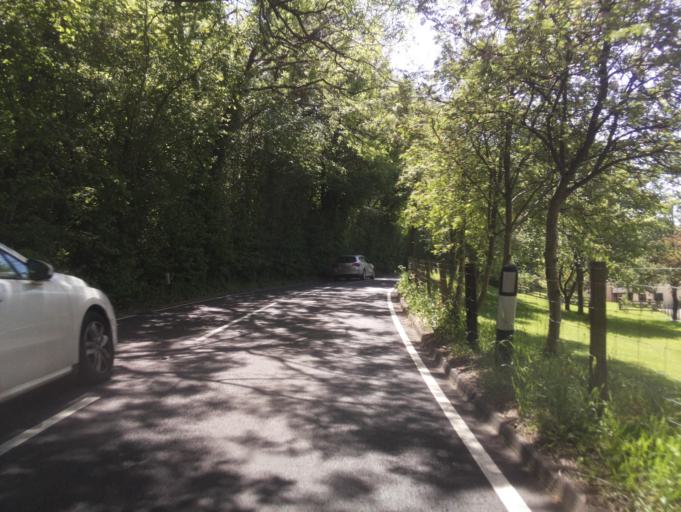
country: GB
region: Wales
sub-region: Monmouthshire
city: Mitchel Troy
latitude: 51.7785
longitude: -2.7274
